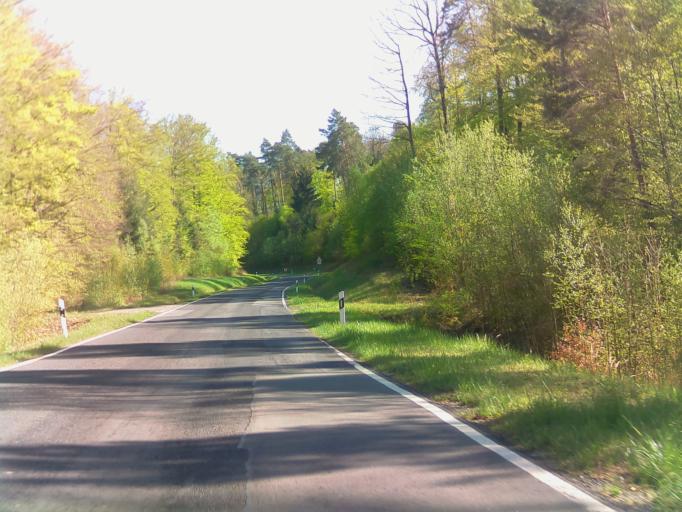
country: DE
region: Bavaria
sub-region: Regierungsbezirk Unterfranken
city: Burgpreppach
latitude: 50.1127
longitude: 10.6403
